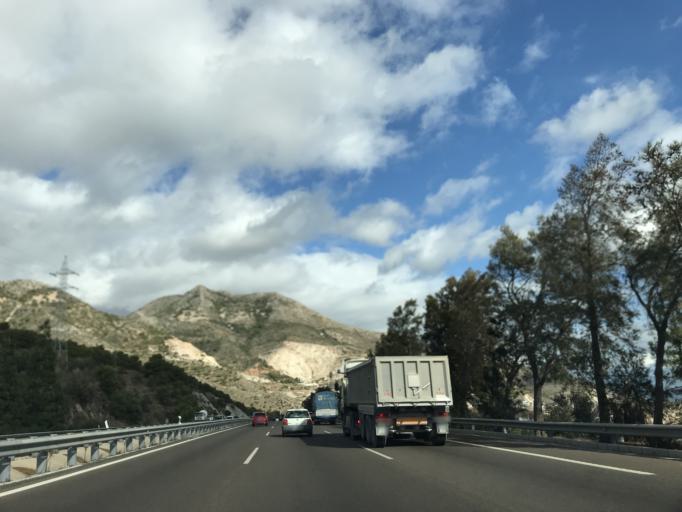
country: ES
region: Andalusia
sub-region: Provincia de Malaga
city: Benalmadena
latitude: 36.5987
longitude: -4.5739
